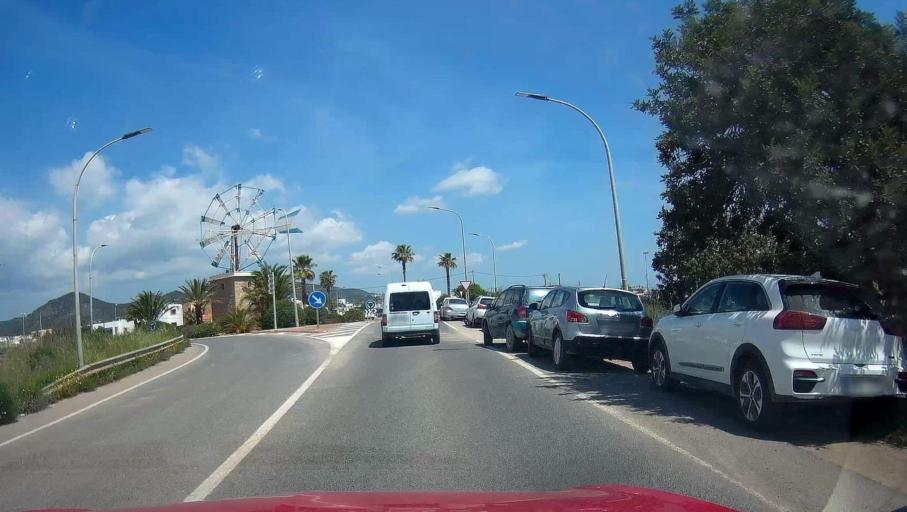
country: ES
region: Balearic Islands
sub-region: Illes Balears
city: Ibiza
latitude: 38.8873
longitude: 1.3955
